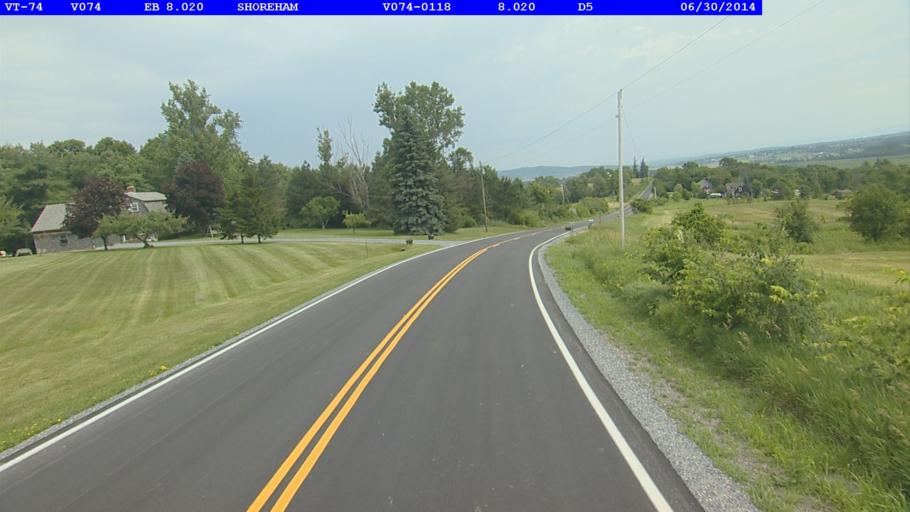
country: US
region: Vermont
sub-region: Addison County
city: Middlebury (village)
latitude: 43.9337
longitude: -73.2873
